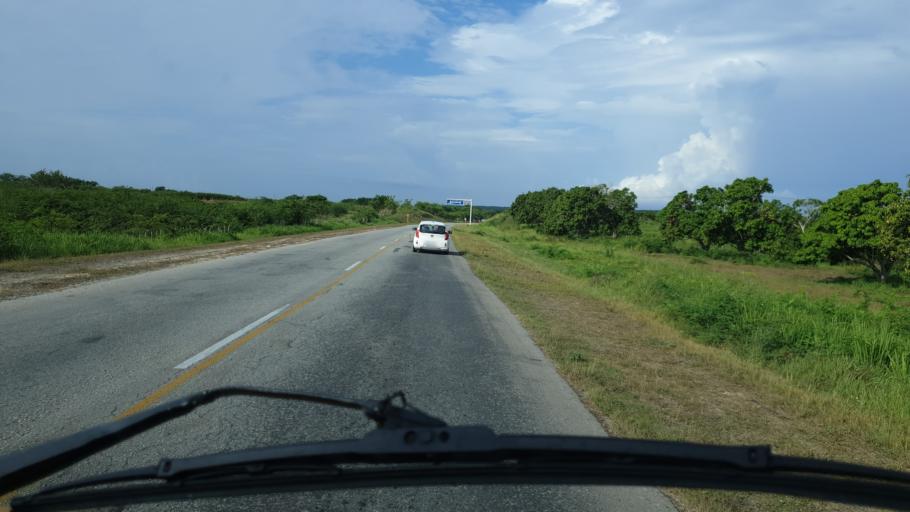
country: CU
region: Cienfuegos
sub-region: Municipio de Cienfuegos
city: Cienfuegos
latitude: 22.0791
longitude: -80.3893
